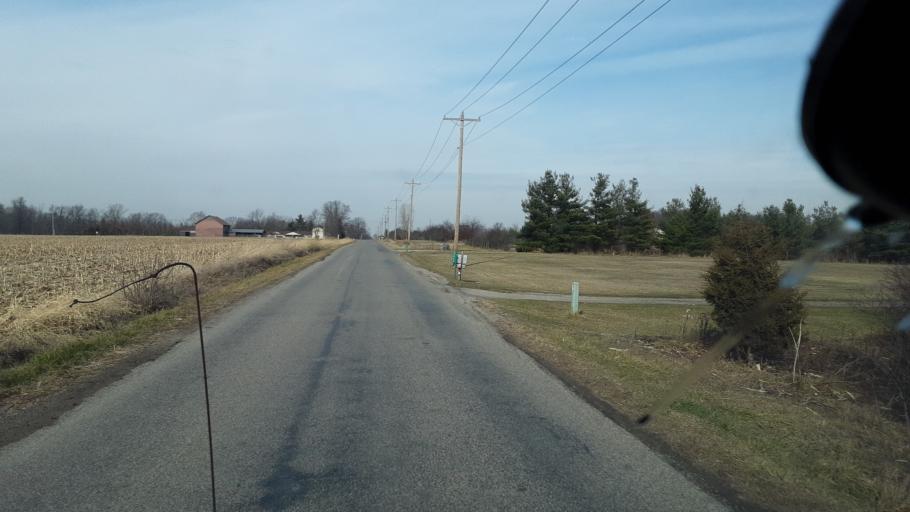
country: US
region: Indiana
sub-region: DeKalb County
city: Butler
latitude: 41.3889
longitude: -84.8889
